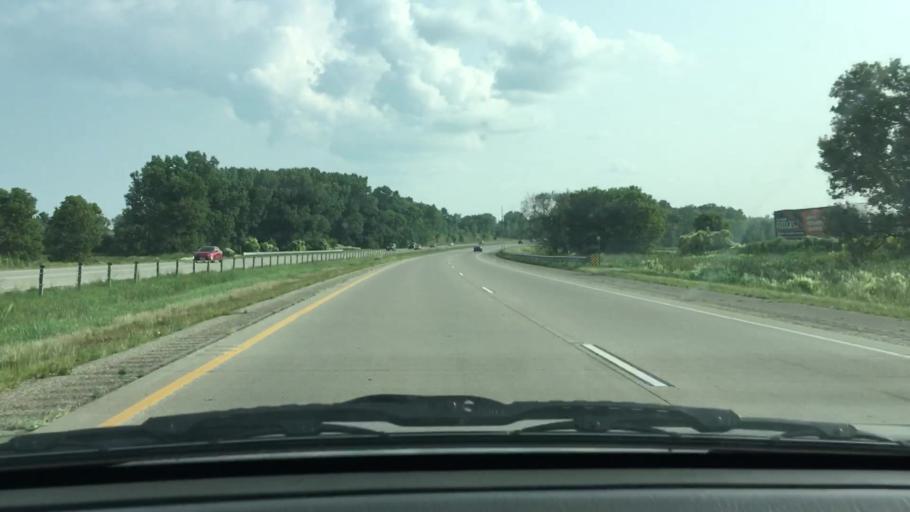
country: US
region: Minnesota
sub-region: Scott County
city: Elko New Market
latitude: 44.6102
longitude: -93.2960
